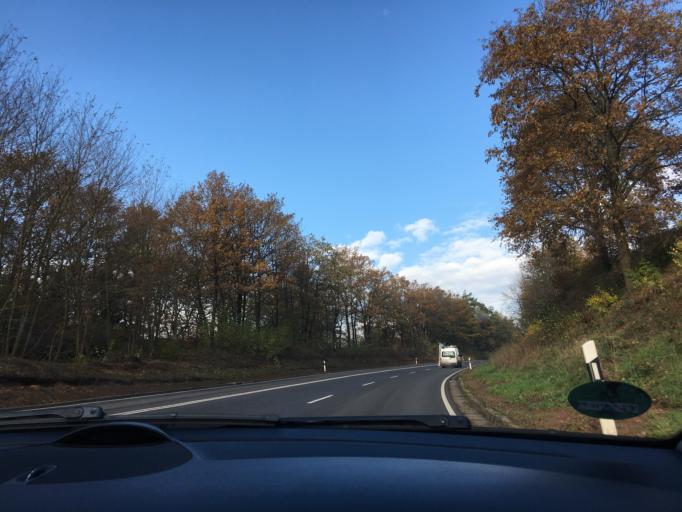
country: DE
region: Rheinland-Pfalz
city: Schopp
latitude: 49.3338
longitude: 7.6715
